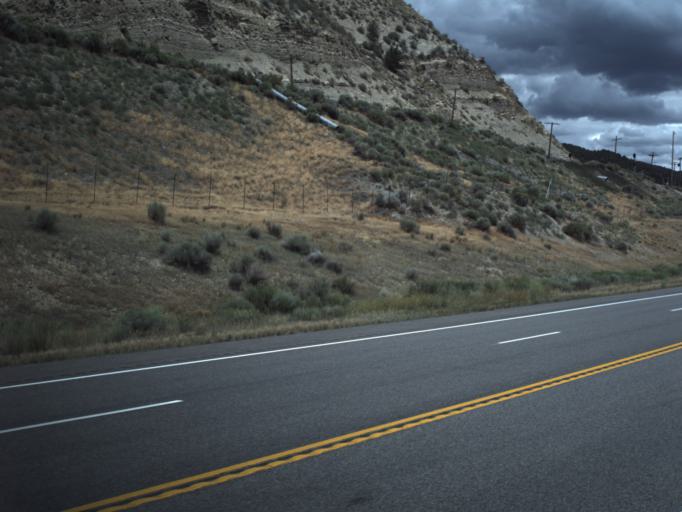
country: US
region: Utah
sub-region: Sanpete County
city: Fairview
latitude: 39.9288
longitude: -111.1836
